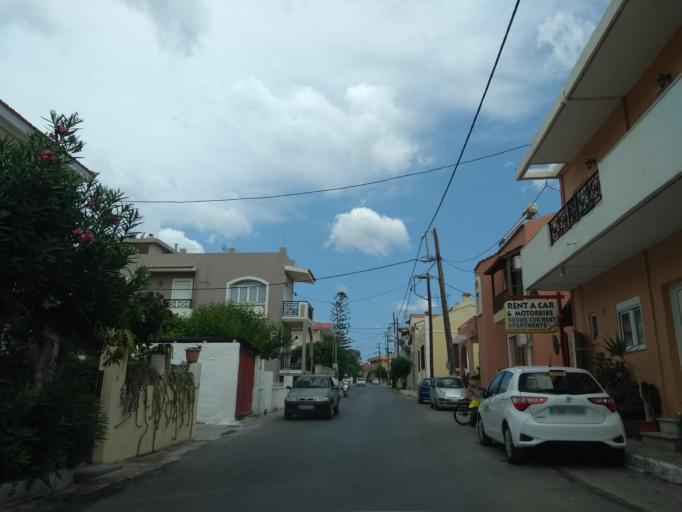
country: GR
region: Crete
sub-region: Nomos Chanias
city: Kalivai
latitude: 35.4565
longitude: 24.1685
